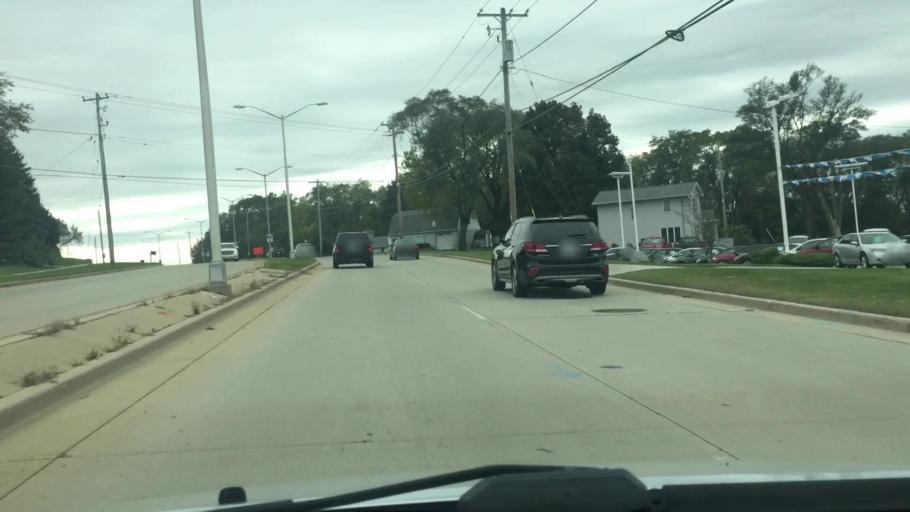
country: US
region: Wisconsin
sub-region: Waukesha County
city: Waukesha
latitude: 43.0251
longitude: -88.1928
